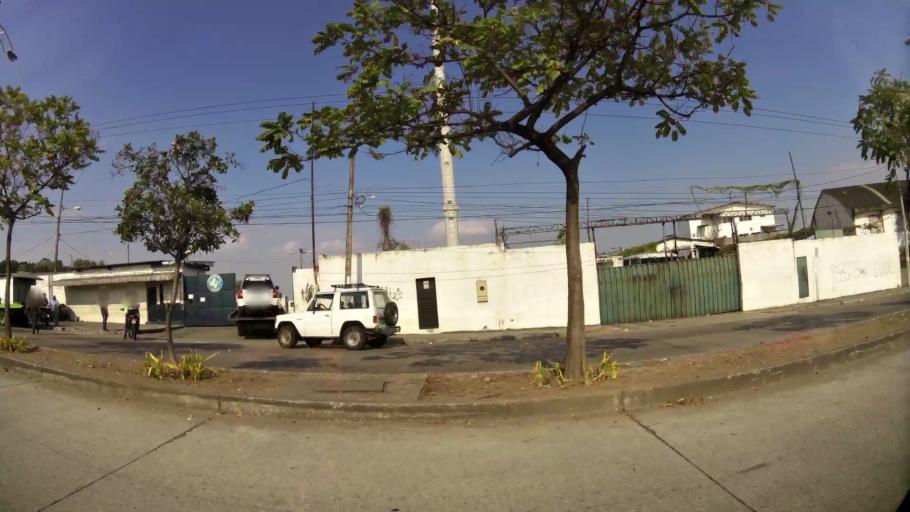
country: EC
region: Guayas
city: Guayaquil
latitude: -2.1400
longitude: -79.9249
